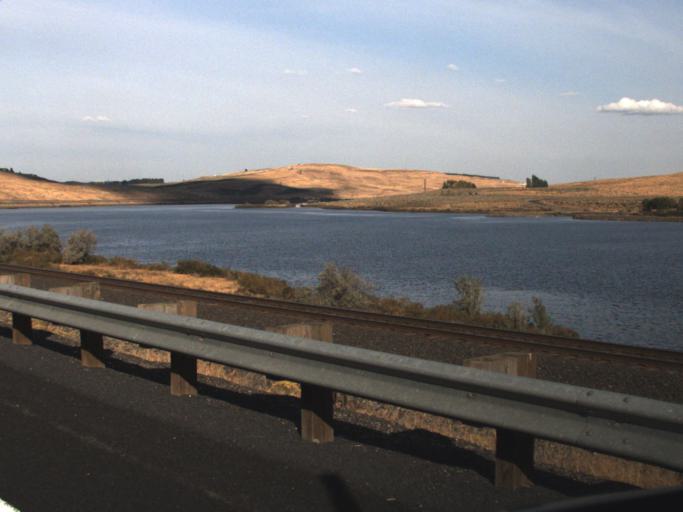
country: US
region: Oregon
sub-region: Morrow County
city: Boardman
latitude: 45.8568
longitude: -119.8606
